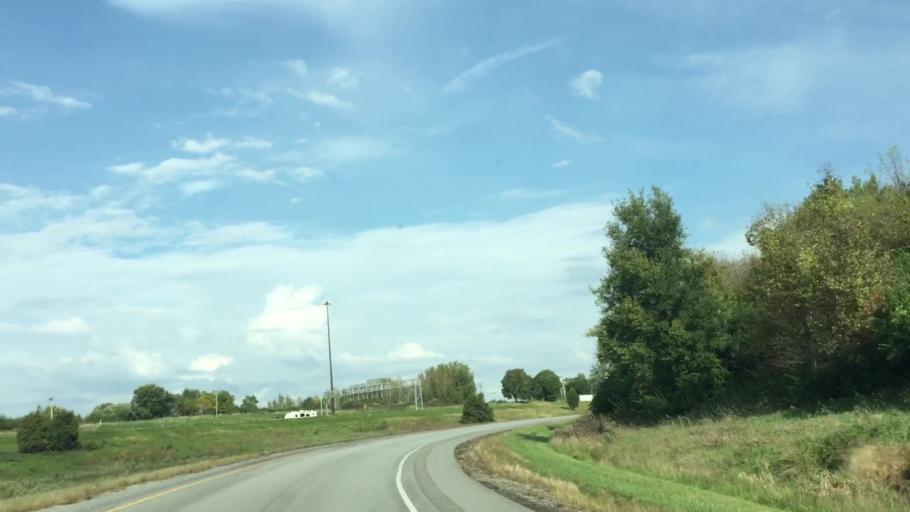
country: US
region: Illinois
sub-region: Henry County
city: Colona
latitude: 41.5387
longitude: -90.3399
